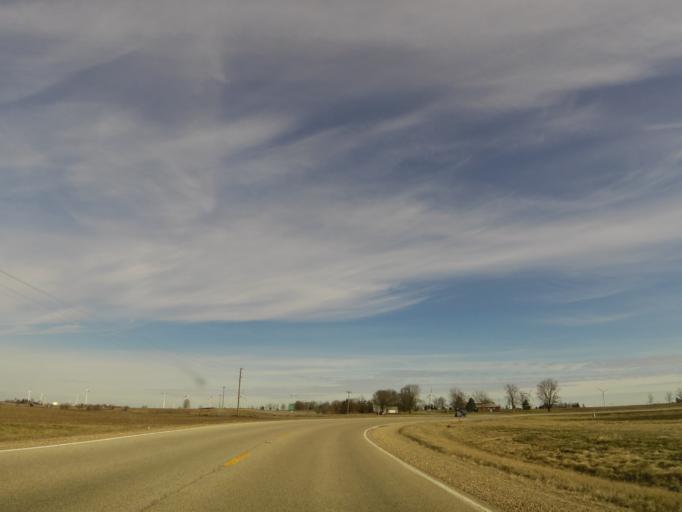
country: US
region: Illinois
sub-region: McLean County
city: Twin Grove
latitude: 40.5344
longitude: -89.0608
